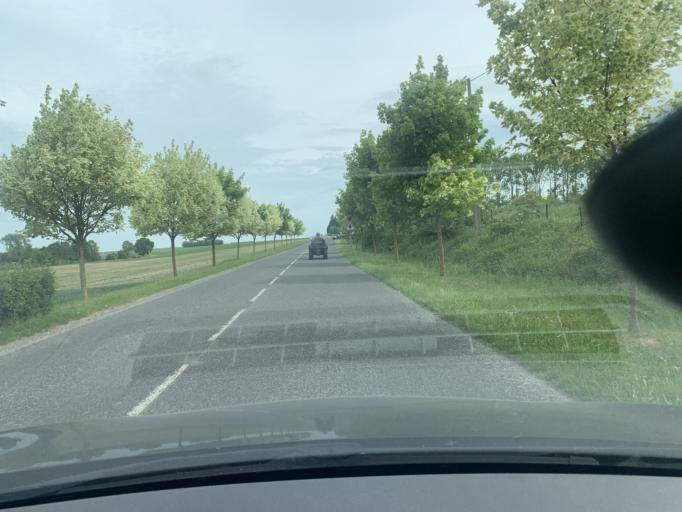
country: FR
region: Nord-Pas-de-Calais
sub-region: Departement du Nord
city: Marcoing
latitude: 50.1291
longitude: 3.1922
